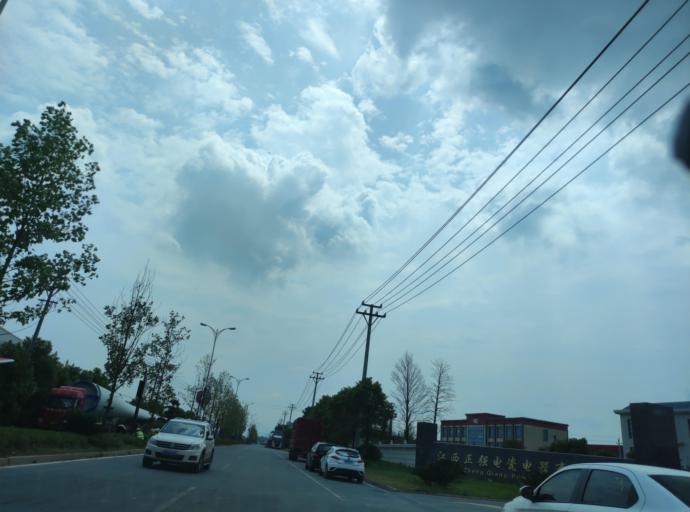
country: CN
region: Jiangxi Sheng
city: Yuannan
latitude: 27.6648
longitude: 114.0153
